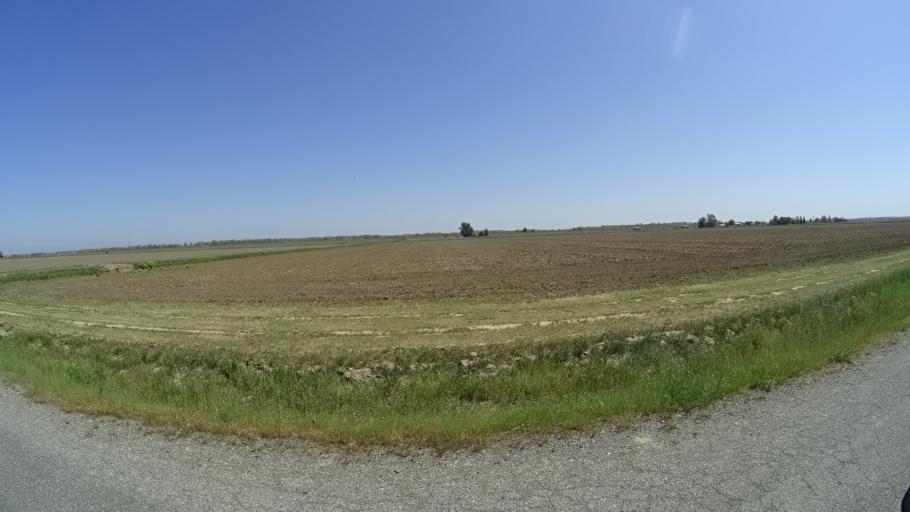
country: US
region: California
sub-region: Glenn County
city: Hamilton City
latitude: 39.5722
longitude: -122.0277
